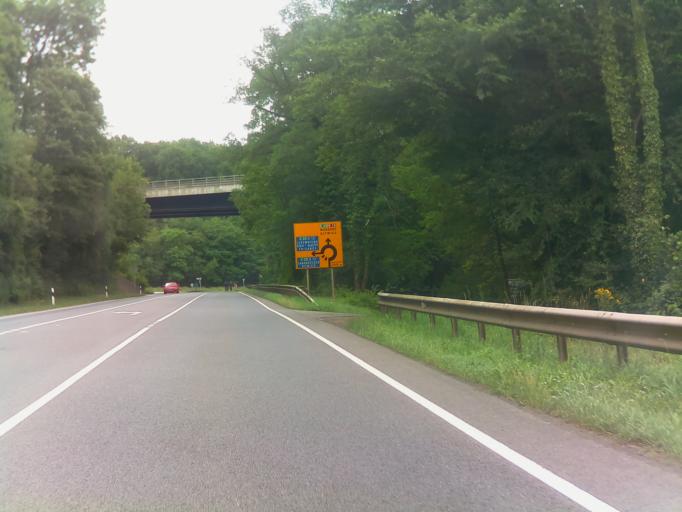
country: LU
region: Luxembourg
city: Aspelt
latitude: 49.5167
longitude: 6.2397
